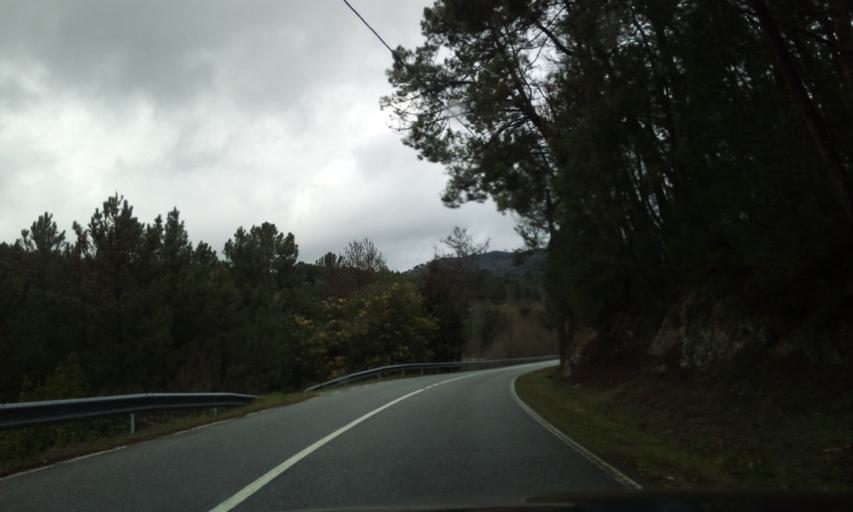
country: PT
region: Guarda
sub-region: Fornos de Algodres
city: Fornos de Algodres
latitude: 40.6094
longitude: -7.5759
